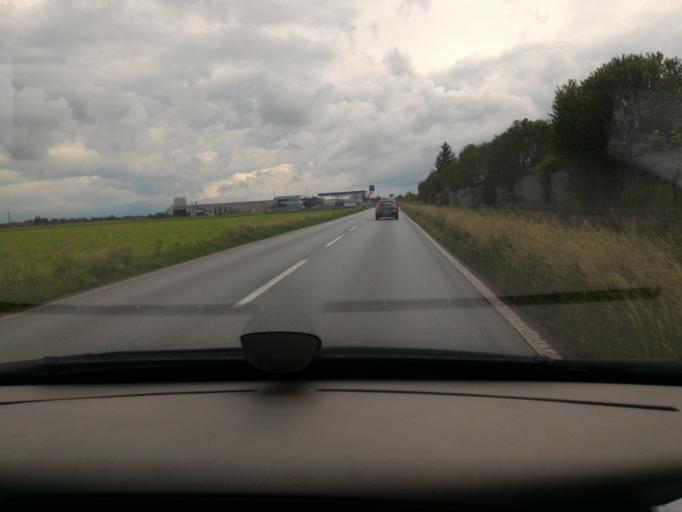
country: IT
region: Piedmont
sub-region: Provincia di Cuneo
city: Genola
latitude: 44.6083
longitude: 7.6619
